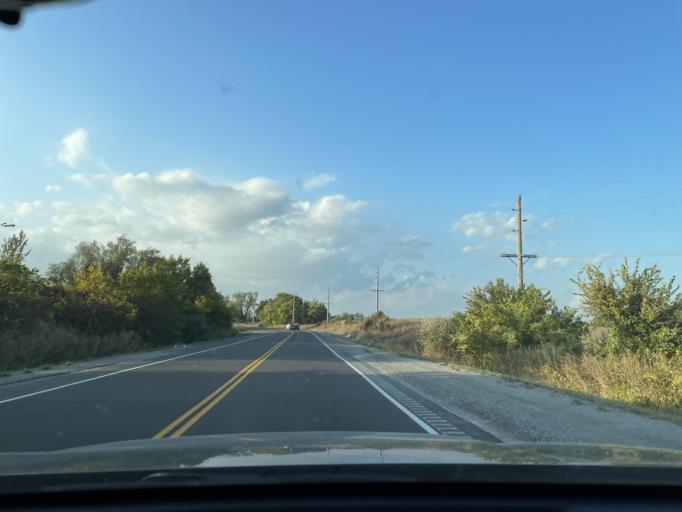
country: US
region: Missouri
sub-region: Andrew County
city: Country Club Village
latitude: 39.8388
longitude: -94.8659
